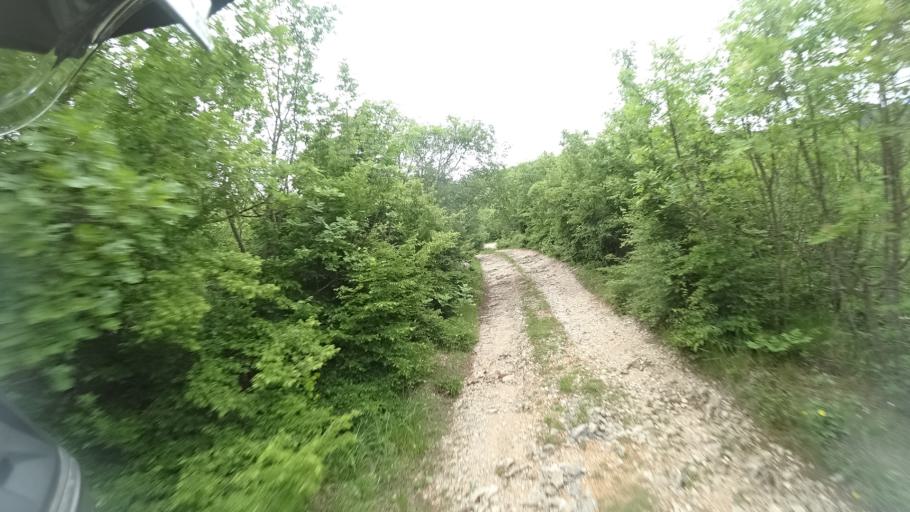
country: HR
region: Splitsko-Dalmatinska
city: Hrvace
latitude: 43.8949
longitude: 16.5434
